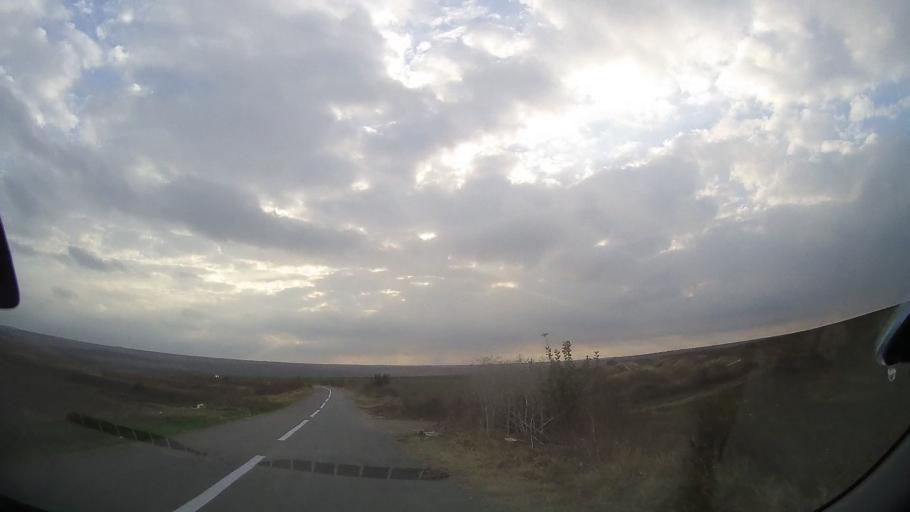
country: RO
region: Constanta
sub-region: Comuna Deleni
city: Pietreni
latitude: 44.1247
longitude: 28.1068
